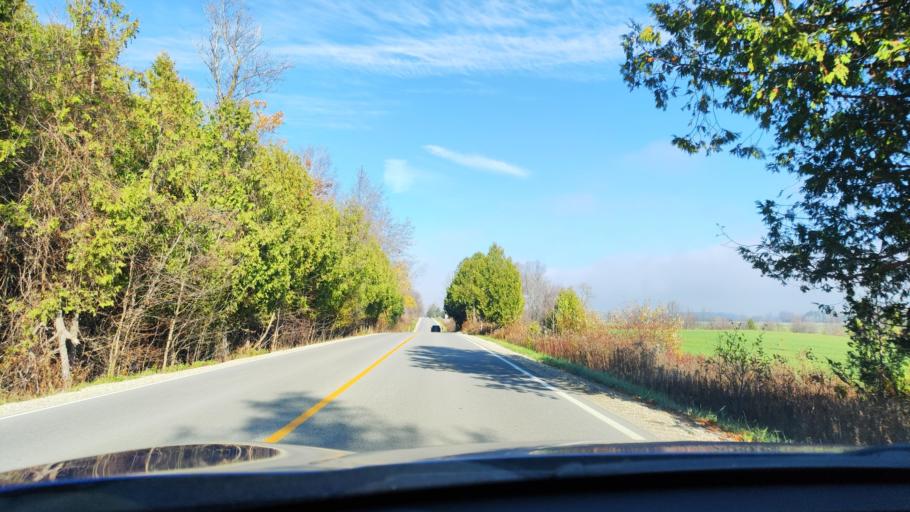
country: CA
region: Ontario
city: Wasaga Beach
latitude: 44.4153
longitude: -80.0613
